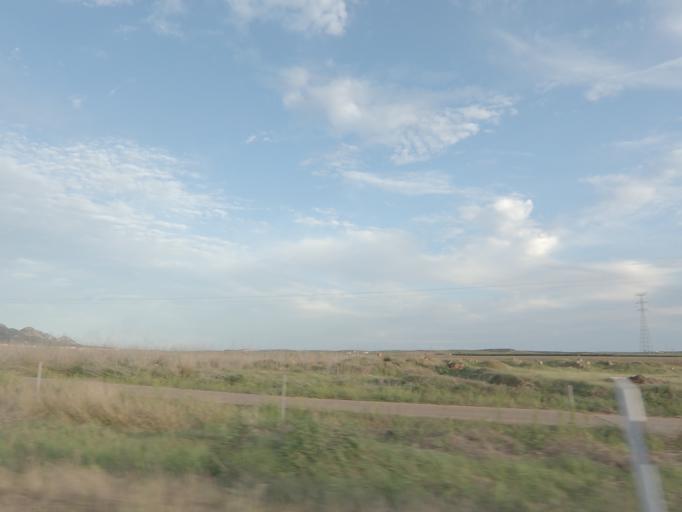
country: ES
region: Extremadura
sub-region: Provincia de Badajoz
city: Arroyo de San Servan
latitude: 38.8708
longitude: -6.4914
